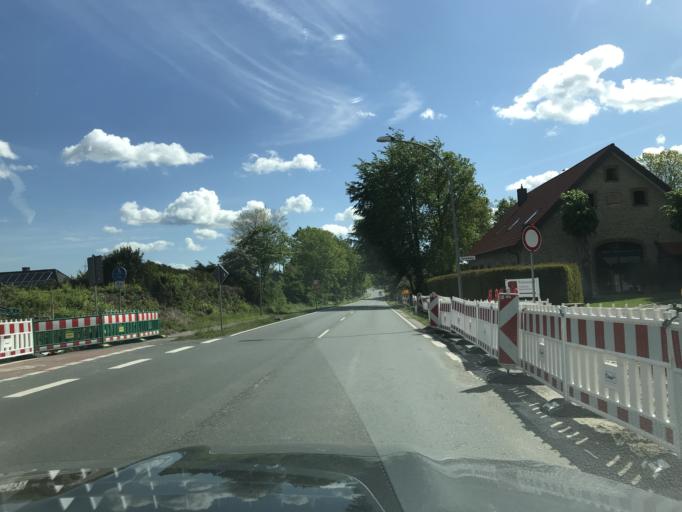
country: DE
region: North Rhine-Westphalia
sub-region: Regierungsbezirk Munster
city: Westerkappeln
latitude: 52.3139
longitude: 7.8886
